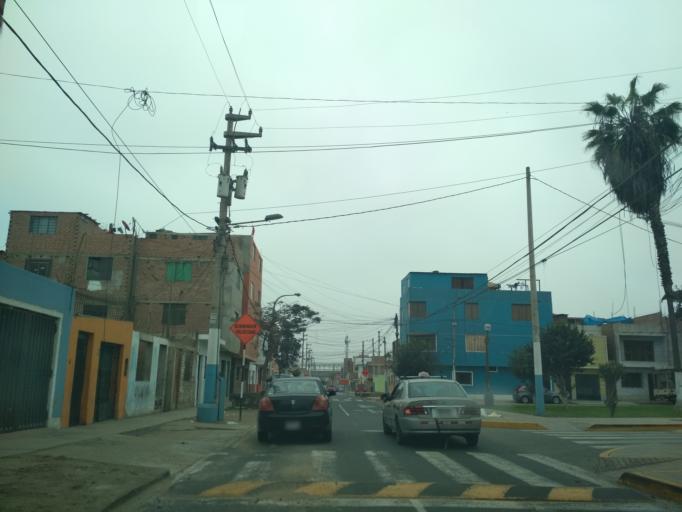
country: PE
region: Callao
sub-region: Callao
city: Callao
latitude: -12.0527
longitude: -77.1041
